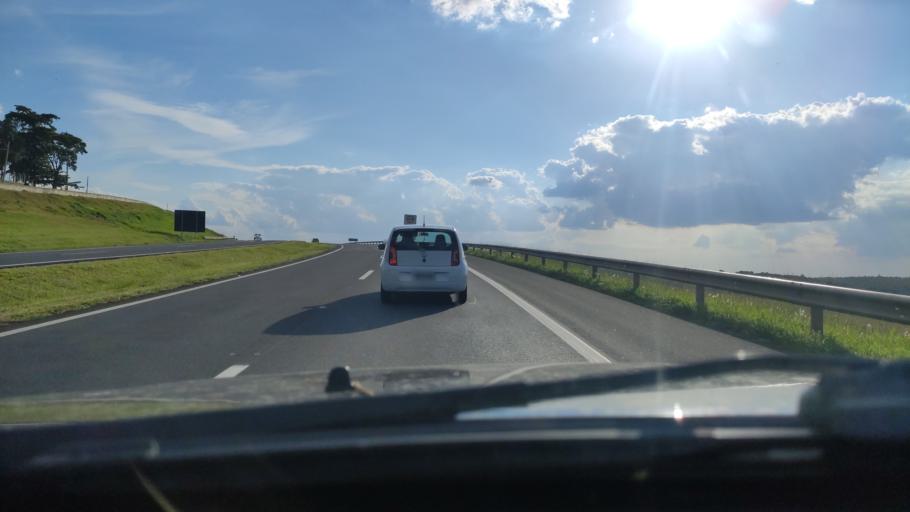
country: BR
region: Sao Paulo
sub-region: Itapira
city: Itapira
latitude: -22.4502
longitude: -46.8481
